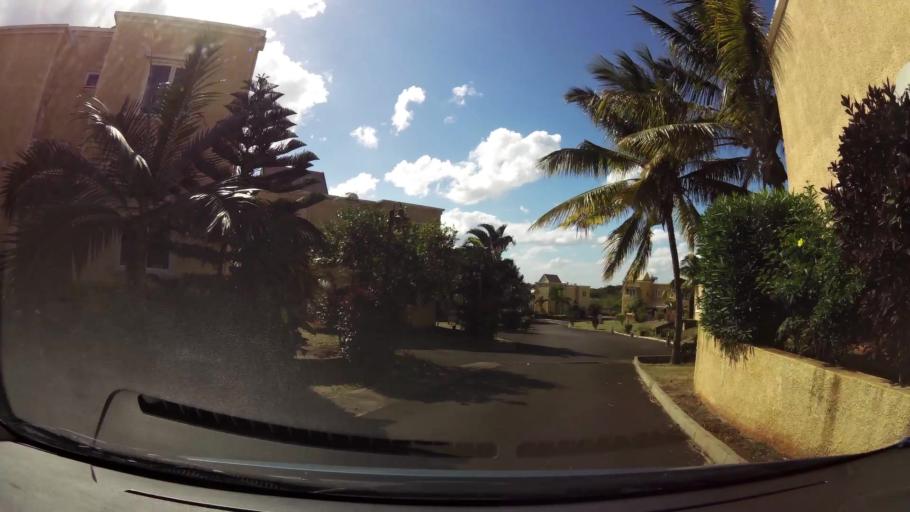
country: MU
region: Black River
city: Albion
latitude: -20.2210
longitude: 57.4144
